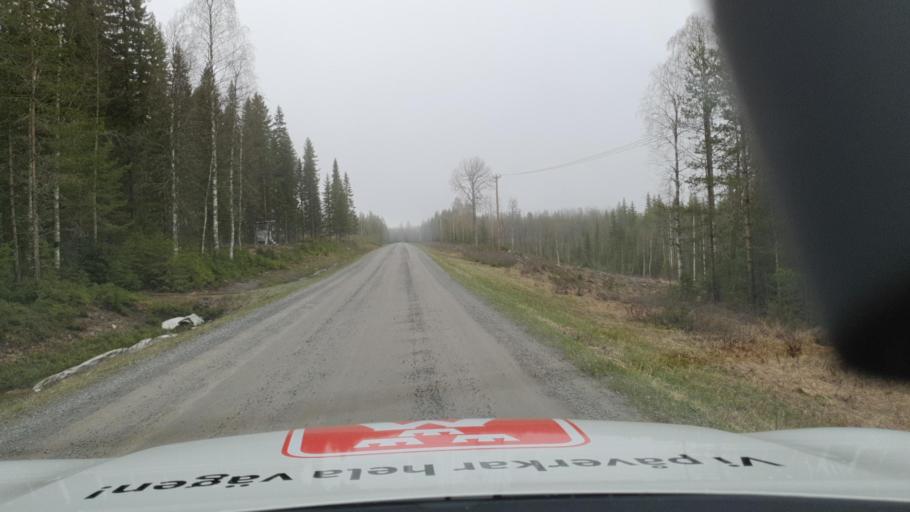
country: SE
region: Vaesterbotten
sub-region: Nordmalings Kommun
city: Nordmaling
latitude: 63.7615
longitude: 19.4834
